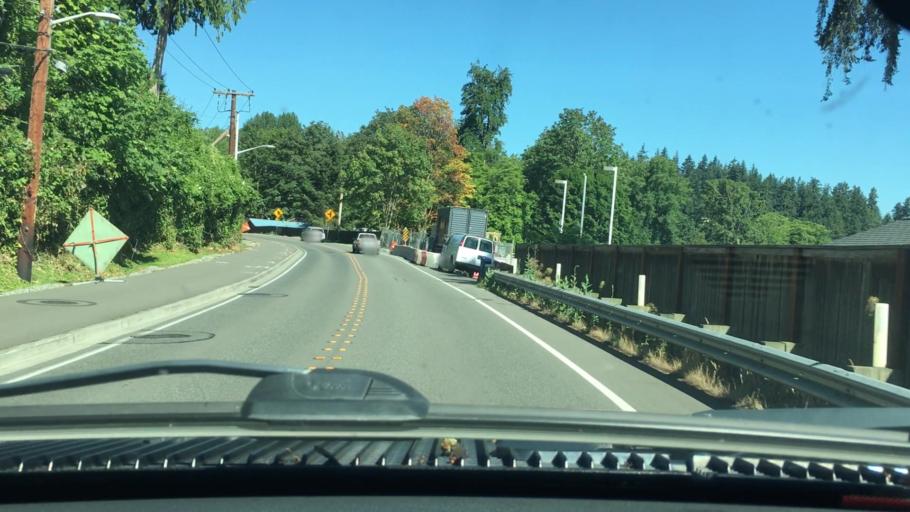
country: US
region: Washington
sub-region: King County
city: West Lake Sammamish
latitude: 47.5758
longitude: -122.1109
